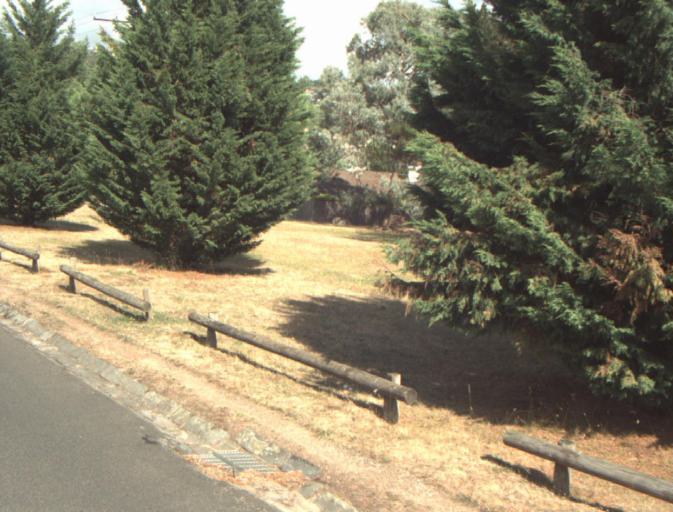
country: AU
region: Tasmania
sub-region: Launceston
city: East Launceston
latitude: -41.4712
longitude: 147.1642
